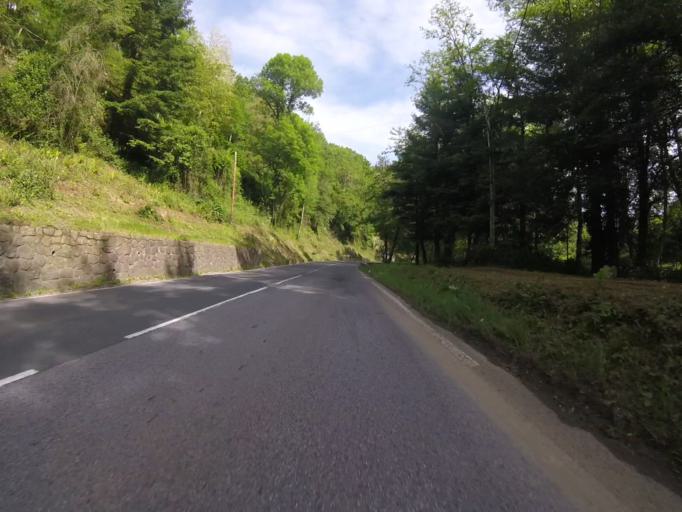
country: ES
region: Basque Country
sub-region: Provincia de Guipuzcoa
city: Azkoitia
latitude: 43.1588
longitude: -2.3347
